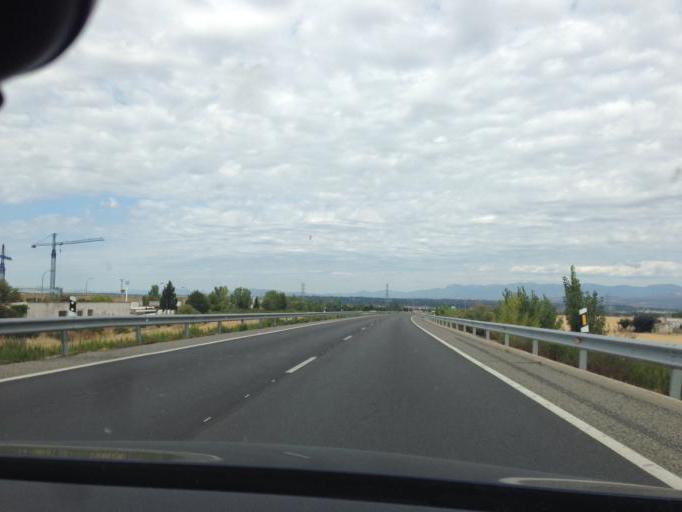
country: ES
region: Madrid
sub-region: Provincia de Madrid
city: Cobena
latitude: 40.5770
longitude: -3.5381
